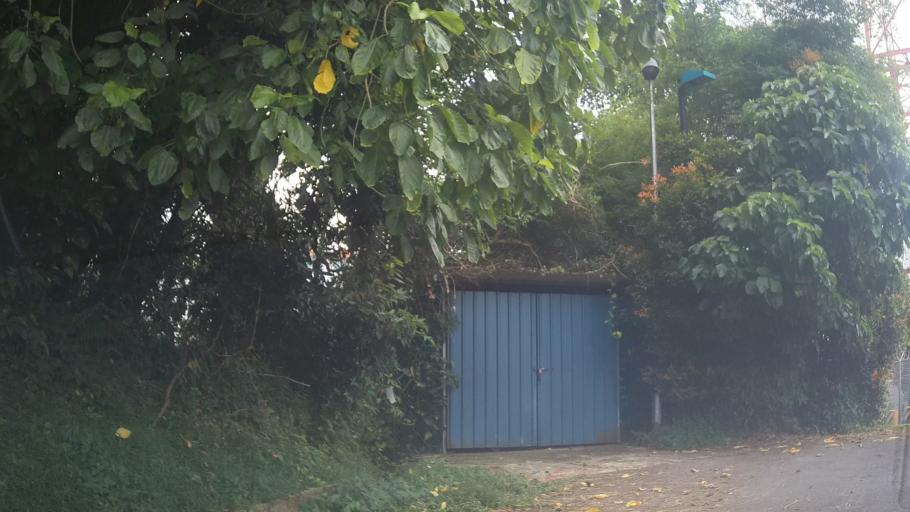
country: SG
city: Singapore
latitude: 1.3531
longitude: 103.7662
